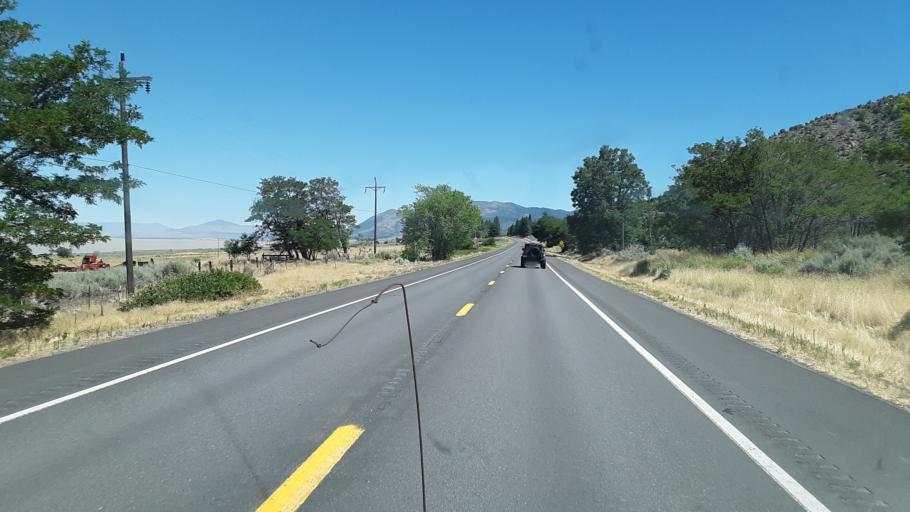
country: US
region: California
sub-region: Lassen County
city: Janesville
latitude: 40.2298
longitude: -120.4417
